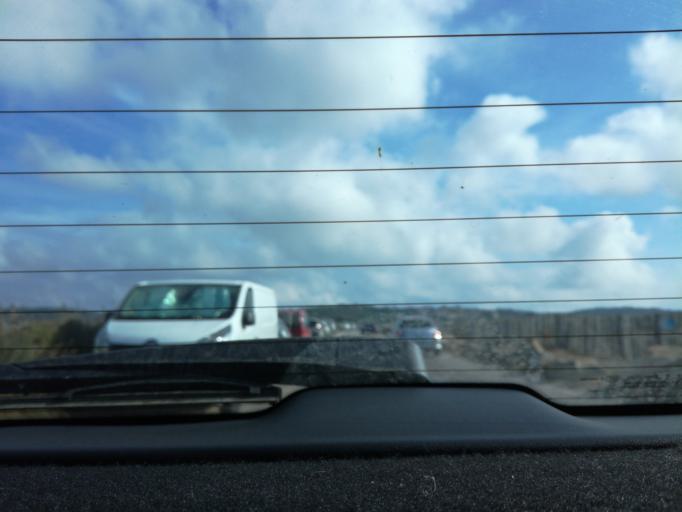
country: FR
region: Provence-Alpes-Cote d'Azur
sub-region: Departement du Var
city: Hyeres
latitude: 43.0556
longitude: 6.1337
